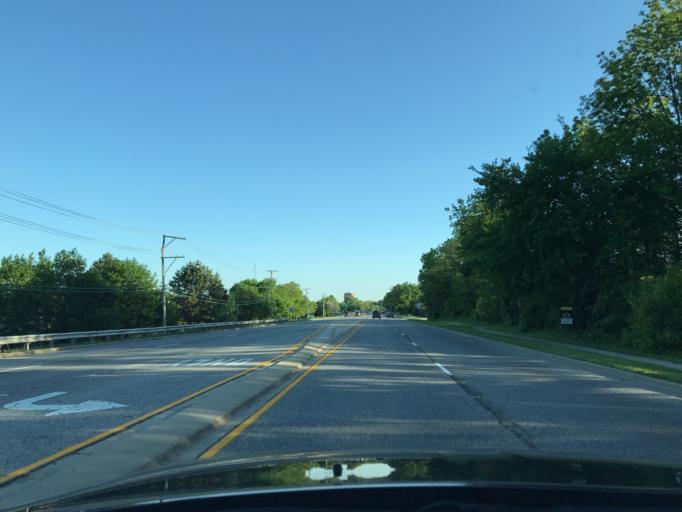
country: US
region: Illinois
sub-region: DuPage County
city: Woodridge
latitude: 41.7637
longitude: -88.0663
